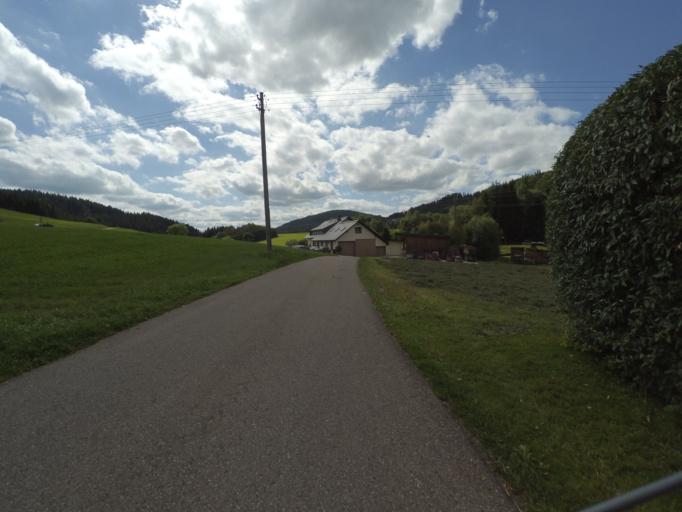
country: DE
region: Baden-Wuerttemberg
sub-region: Freiburg Region
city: Titisee-Neustadt
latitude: 47.9368
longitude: 8.1996
